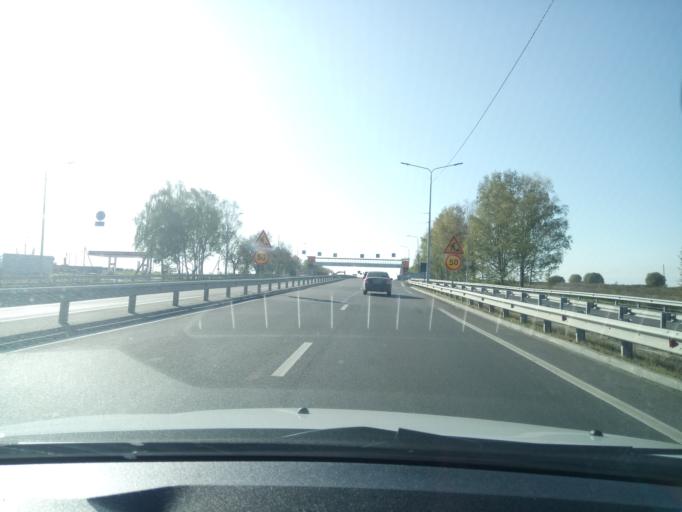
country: RU
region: Nizjnij Novgorod
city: Burevestnik
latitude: 56.0026
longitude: 43.9672
